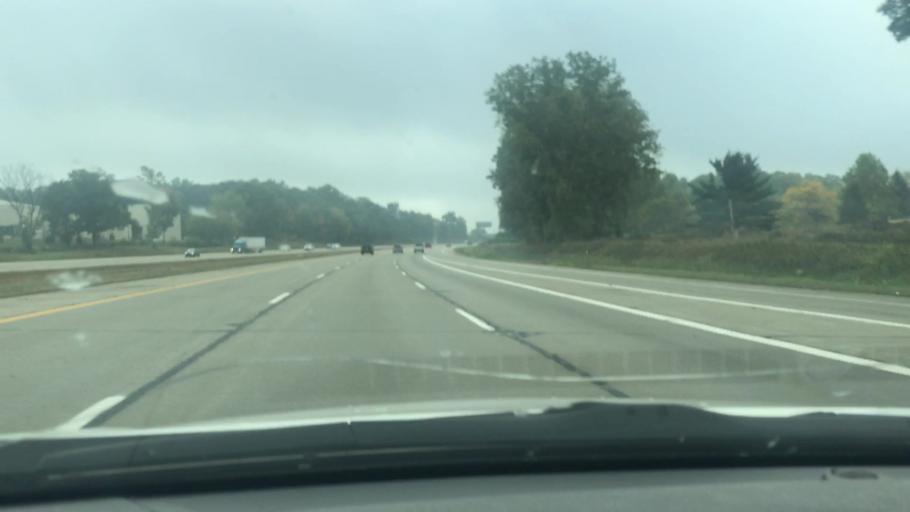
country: US
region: Michigan
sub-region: Livingston County
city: Howell
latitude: 42.6040
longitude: -83.9539
